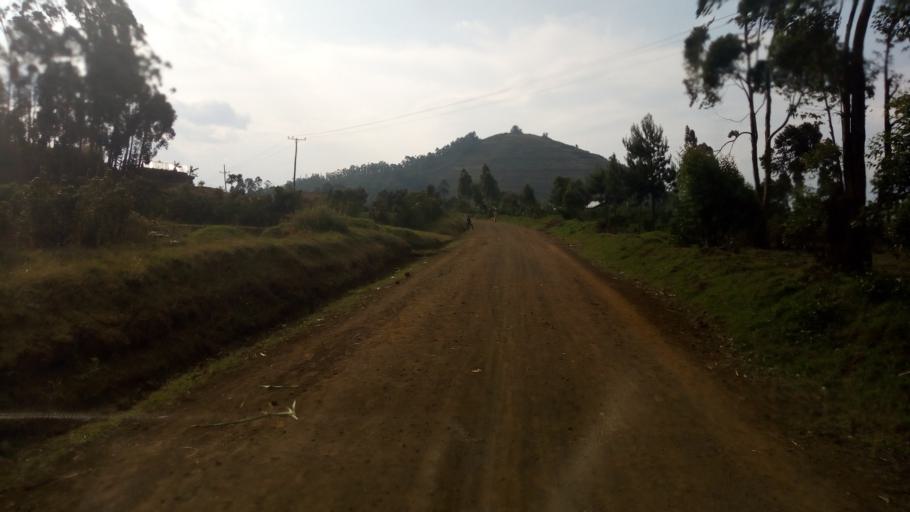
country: UG
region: Western Region
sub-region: Kisoro District
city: Kisoro
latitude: -1.3039
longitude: 29.7093
